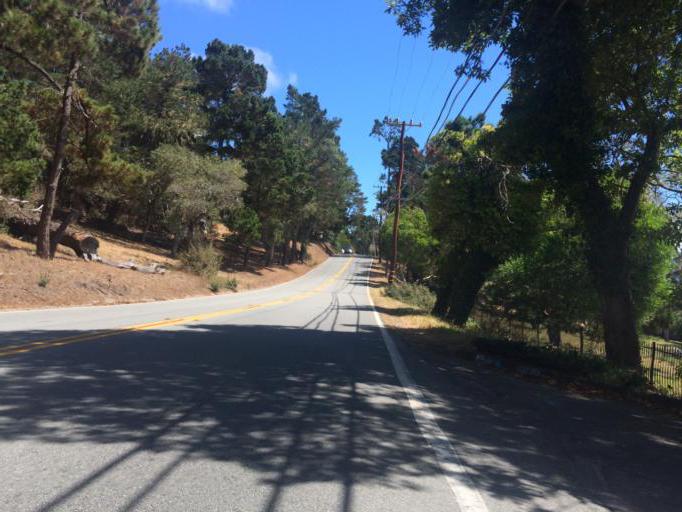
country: US
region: California
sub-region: Monterey County
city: Carmel-by-the-Sea
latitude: 36.5625
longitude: -121.9300
